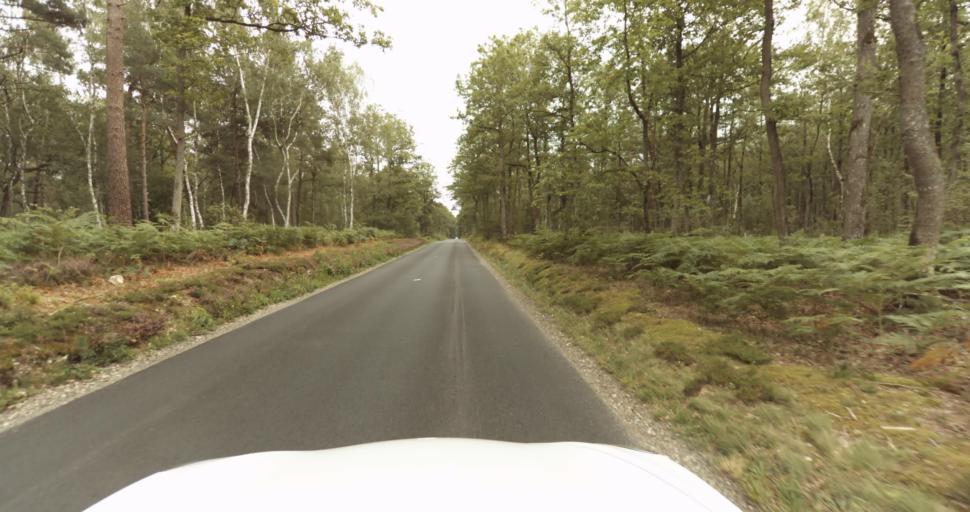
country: FR
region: Haute-Normandie
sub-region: Departement de l'Eure
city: Saint-Sebastien-de-Morsent
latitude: 48.9845
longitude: 1.0655
